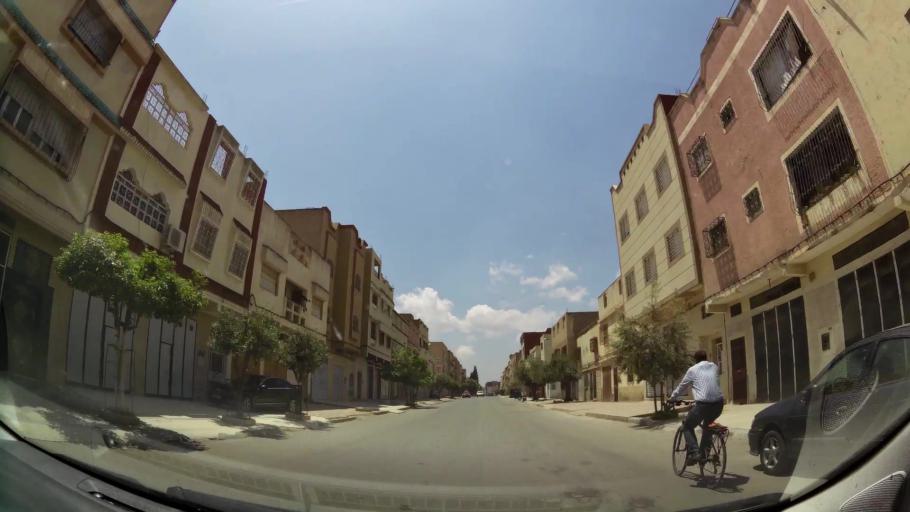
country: MA
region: Oriental
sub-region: Oujda-Angad
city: Oujda
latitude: 34.6982
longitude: -1.8973
